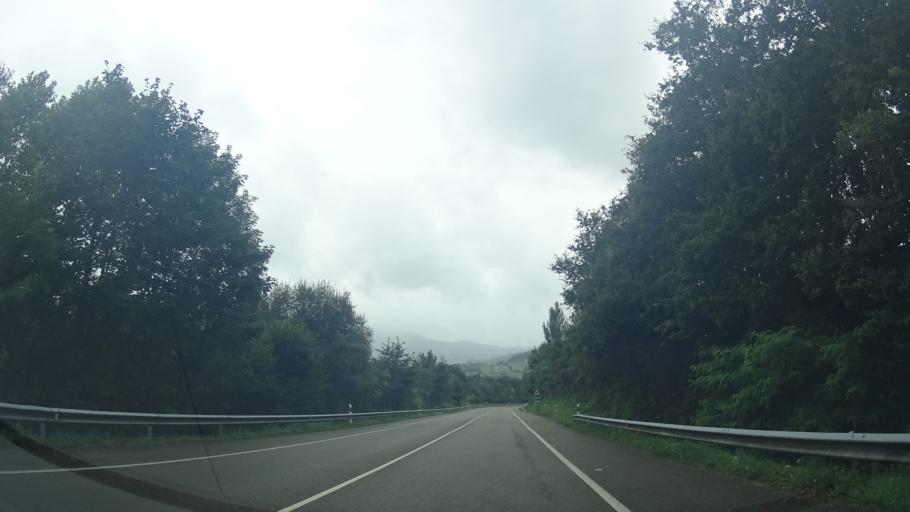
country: ES
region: Asturias
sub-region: Province of Asturias
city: Parres
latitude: 43.3797
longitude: -5.1808
